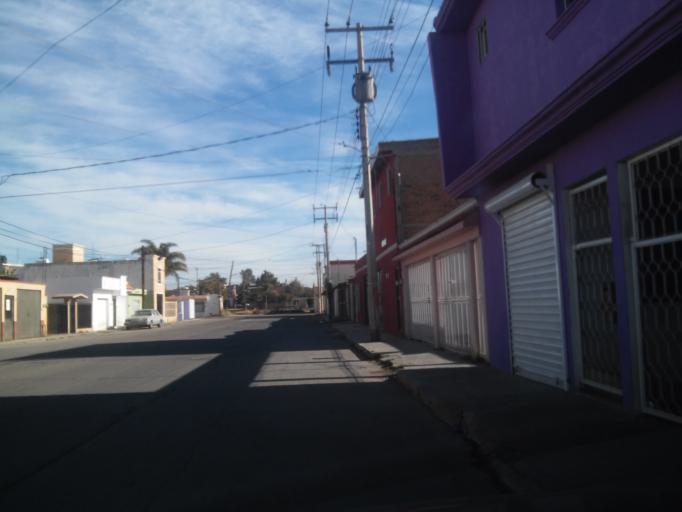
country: MX
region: Durango
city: Victoria de Durango
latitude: 24.0427
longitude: -104.6527
